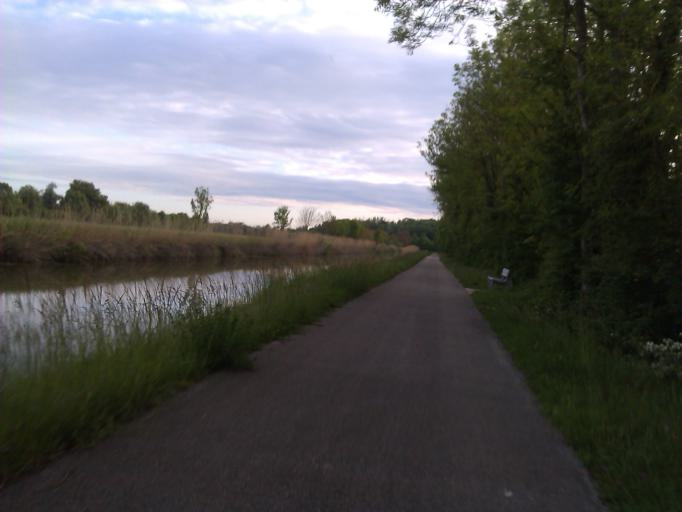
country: FR
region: Franche-Comte
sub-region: Departement du Jura
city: Dole
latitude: 47.1178
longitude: 5.5541
